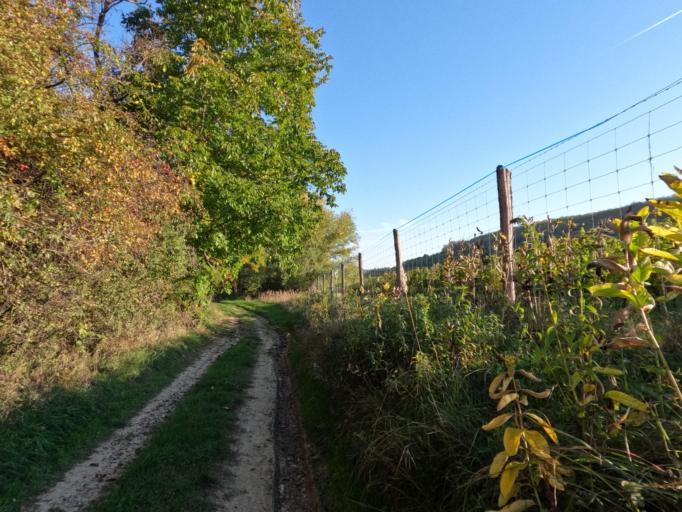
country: HU
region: Tolna
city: Szekszard
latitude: 46.3033
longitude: 18.6585
